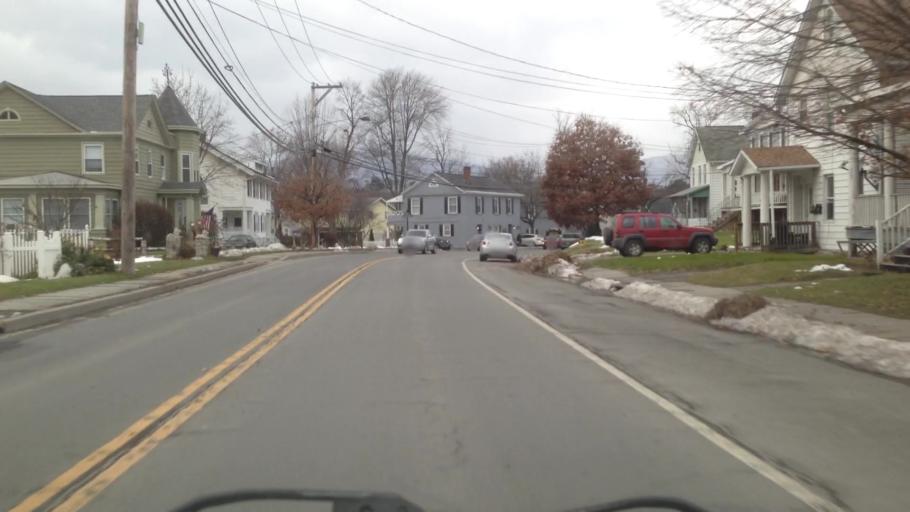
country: US
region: New York
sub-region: Ulster County
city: Saugerties
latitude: 42.0792
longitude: -73.9573
